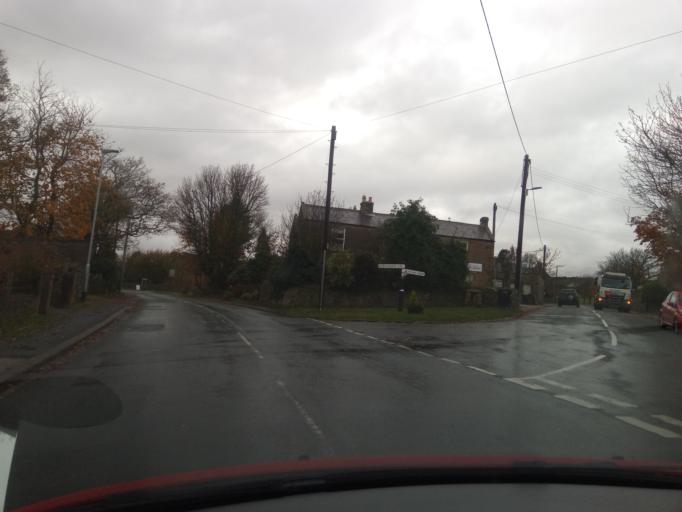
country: GB
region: England
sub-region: County Durham
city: Muggleswick
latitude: 54.8454
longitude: -1.9742
